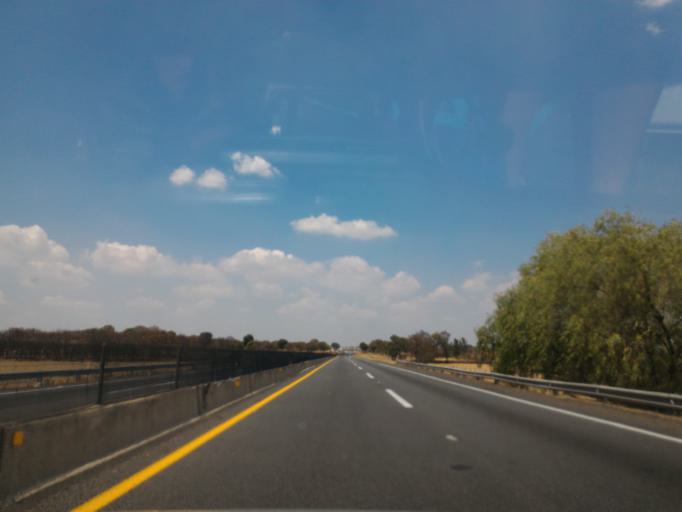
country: MX
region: Jalisco
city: Tepatitlan de Morelos
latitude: 20.8630
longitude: -102.7613
